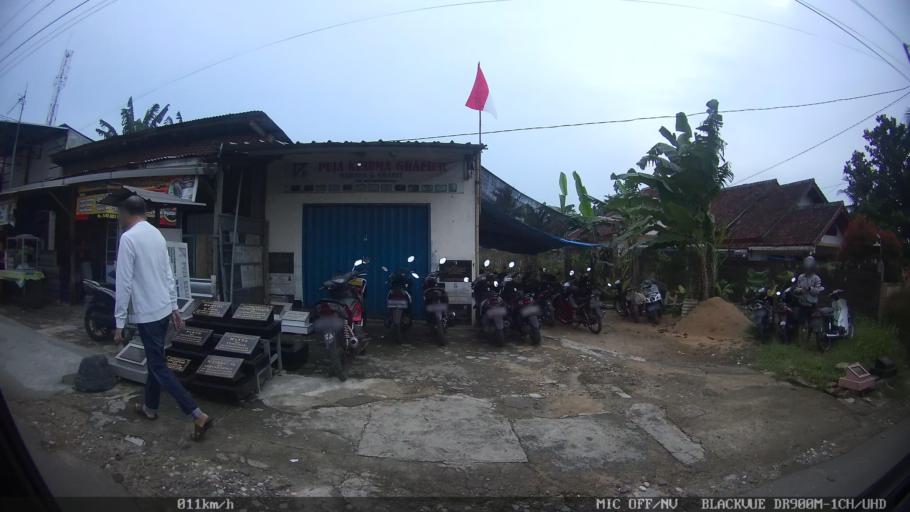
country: ID
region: Lampung
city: Kedaton
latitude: -5.4028
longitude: 105.2349
